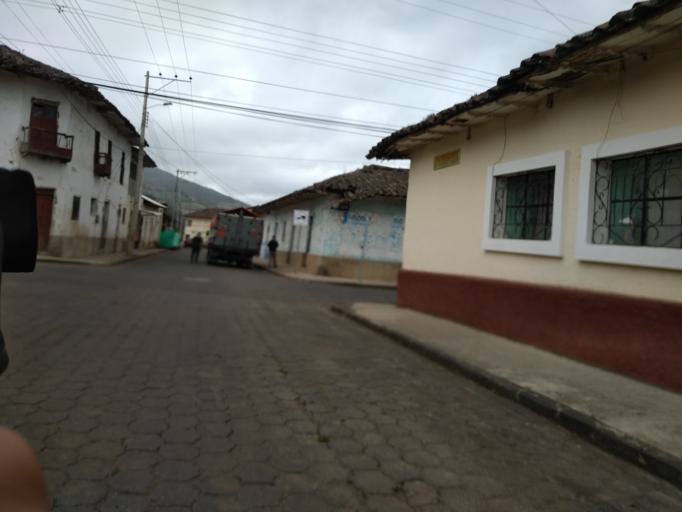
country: EC
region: Carchi
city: El Angel
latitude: 0.6226
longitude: -77.9383
